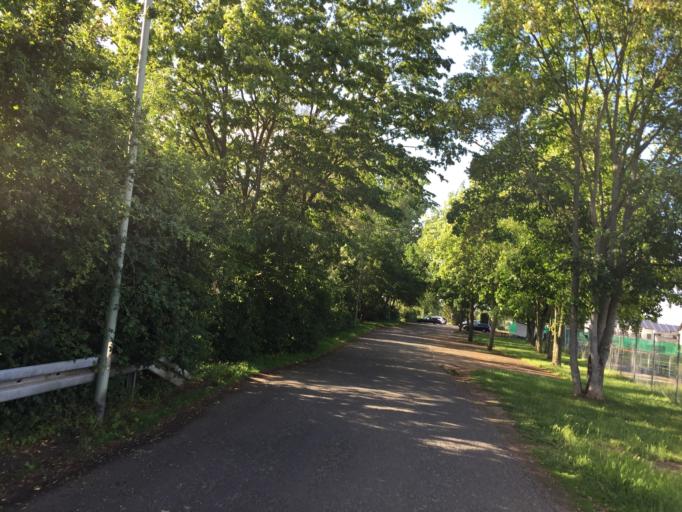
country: DE
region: Hesse
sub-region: Regierungsbezirk Darmstadt
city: Karben
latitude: 50.2238
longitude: 8.7690
